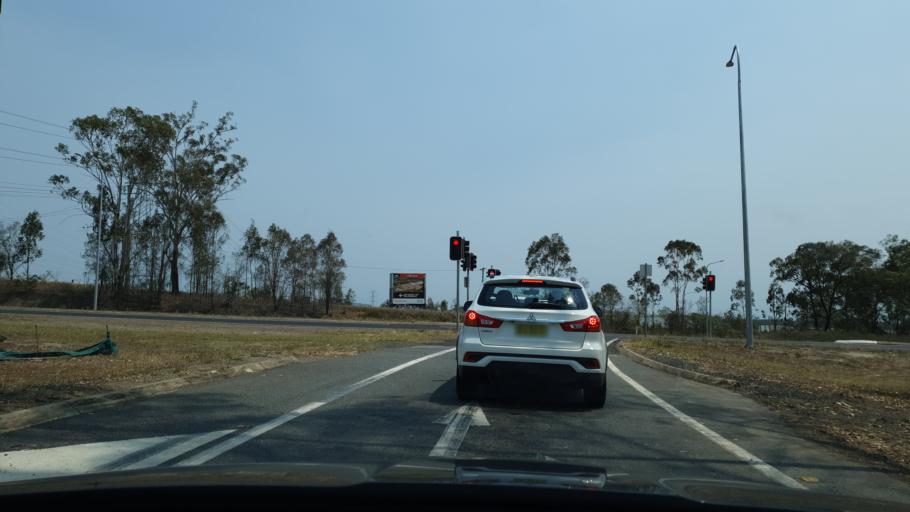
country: AU
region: Queensland
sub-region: Ipswich
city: Bundamba
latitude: -27.6320
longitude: 152.8155
